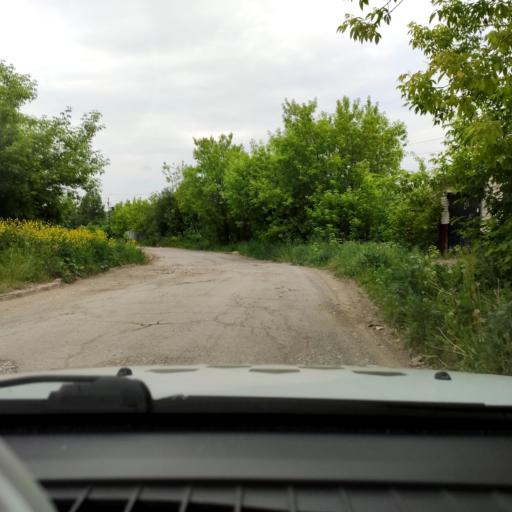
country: RU
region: Perm
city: Perm
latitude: 57.9743
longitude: 56.2877
